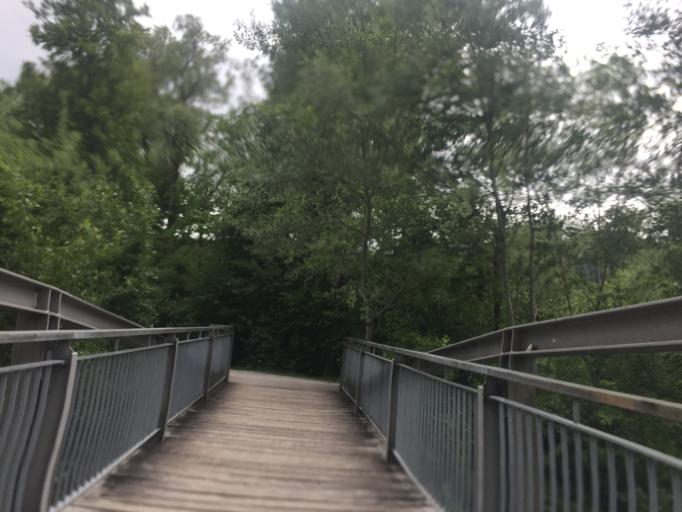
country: CH
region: Bern
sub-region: Bern-Mittelland District
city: Rubigen
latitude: 46.8889
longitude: 7.5384
